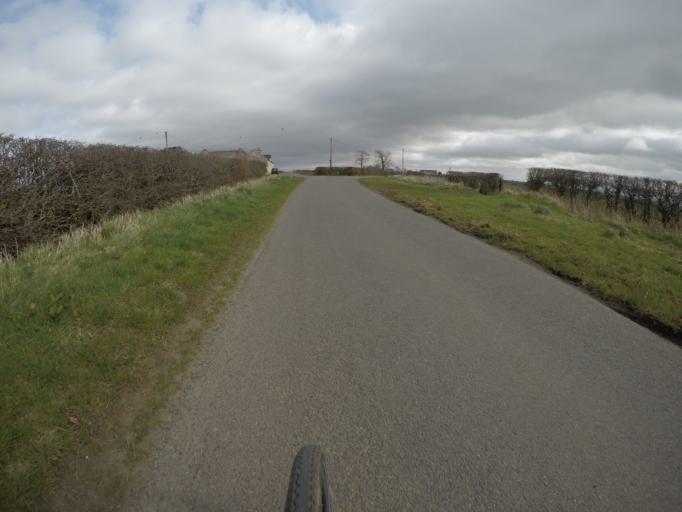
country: GB
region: Scotland
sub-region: North Ayrshire
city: Springside
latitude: 55.6684
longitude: -4.5861
